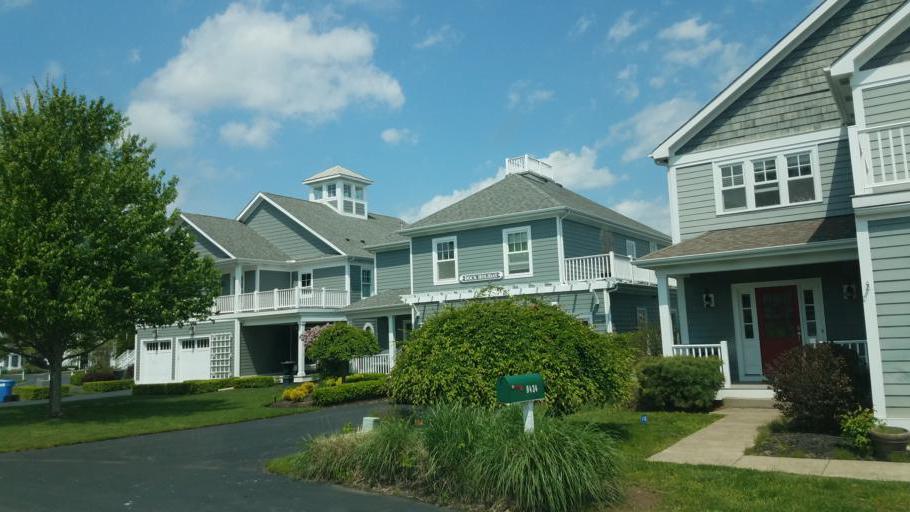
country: US
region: Ohio
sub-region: Perry County
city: Thornport
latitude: 39.9201
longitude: -82.4160
